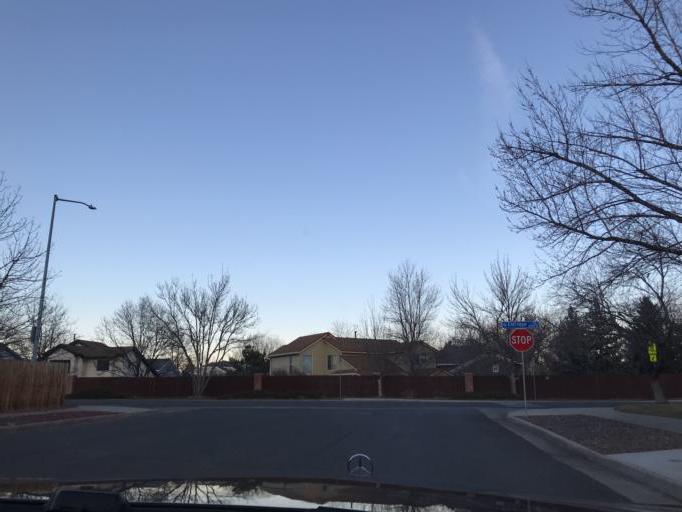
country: US
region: Colorado
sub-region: Jefferson County
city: Applewood
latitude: 39.8241
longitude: -105.1572
